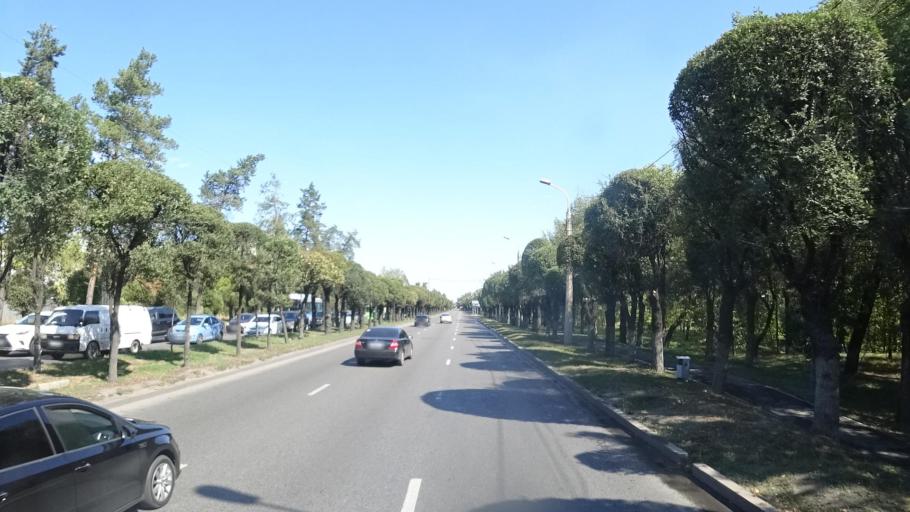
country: KZ
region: Almaty Oblysy
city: Pervomayskiy
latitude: 43.3230
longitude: 76.9737
